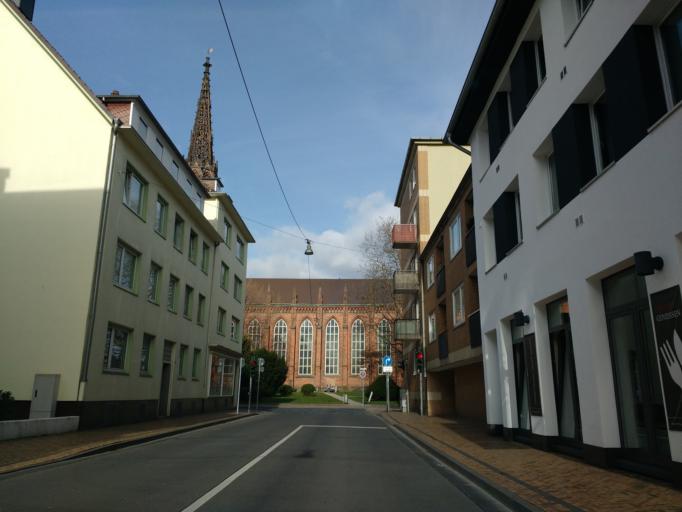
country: DE
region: Bremen
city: Bremerhaven
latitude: 53.5435
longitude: 8.5804
